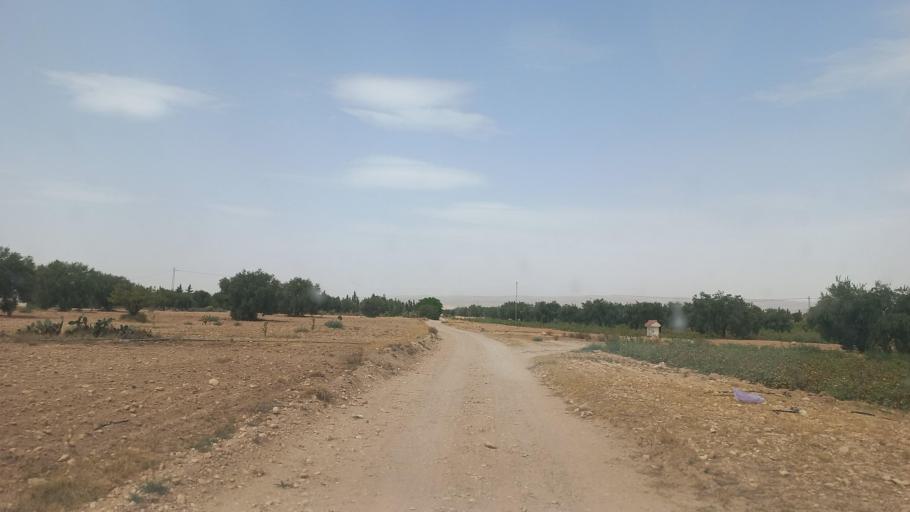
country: TN
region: Al Qasrayn
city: Kasserine
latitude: 35.2570
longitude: 9.0034
